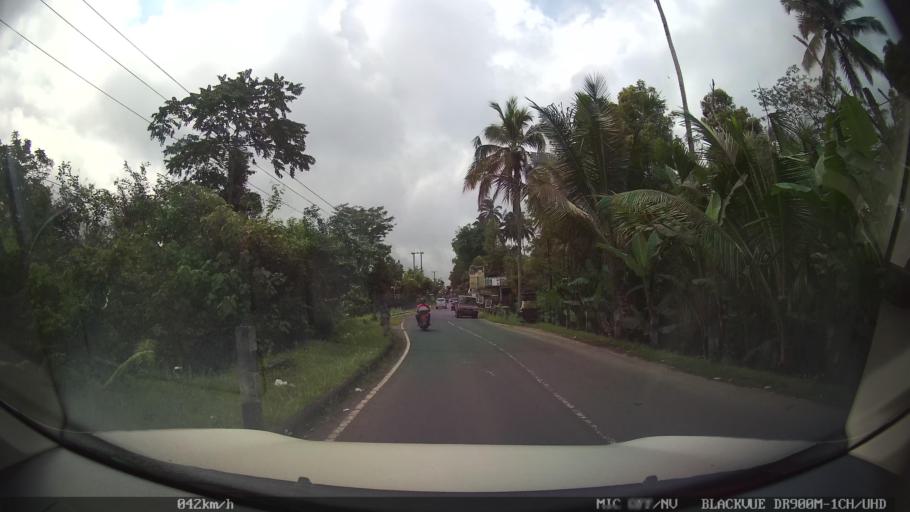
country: ID
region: Bali
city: Petang
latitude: -8.3776
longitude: 115.2236
